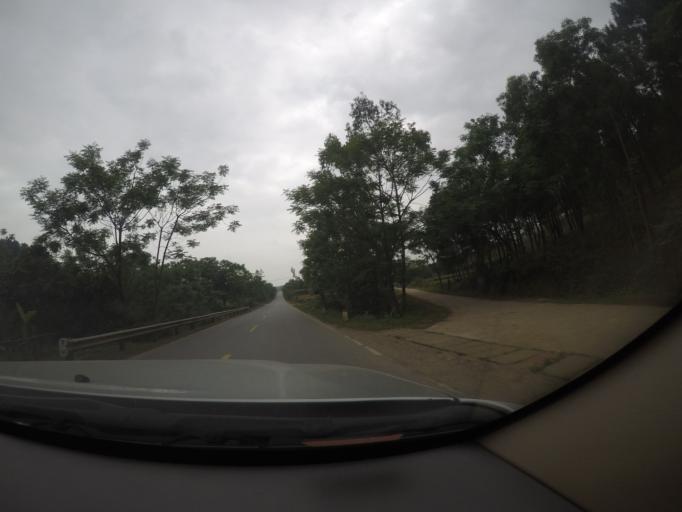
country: VN
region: Quang Binh
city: Hoan Lao
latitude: 17.5987
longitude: 106.4195
